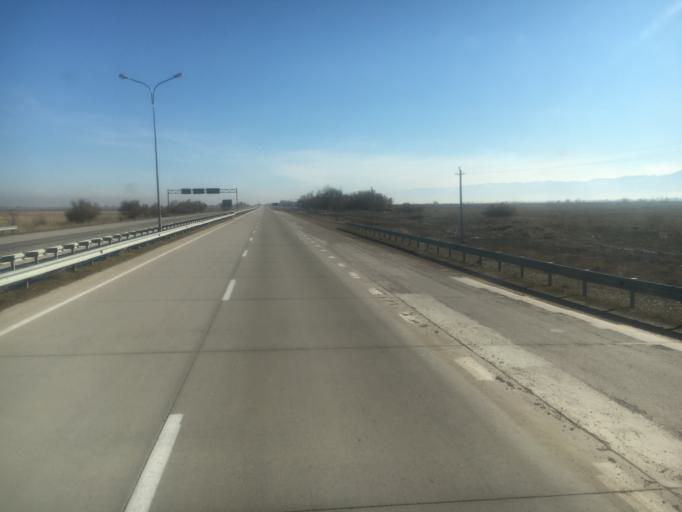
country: KZ
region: Zhambyl
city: Oytal
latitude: 42.9281
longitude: 73.2453
